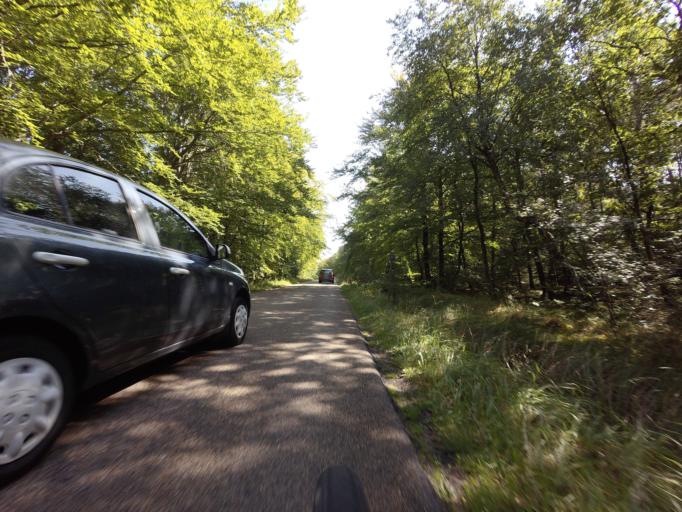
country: DK
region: North Denmark
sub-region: Hjorring Kommune
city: Hirtshals
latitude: 57.5831
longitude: 9.9966
